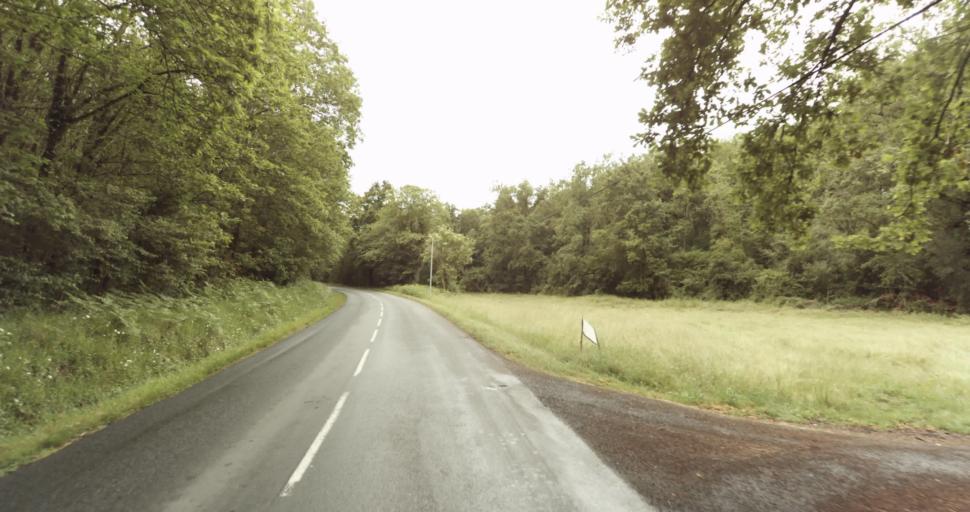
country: FR
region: Aquitaine
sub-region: Departement de la Dordogne
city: Belves
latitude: 44.7149
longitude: 0.9348
